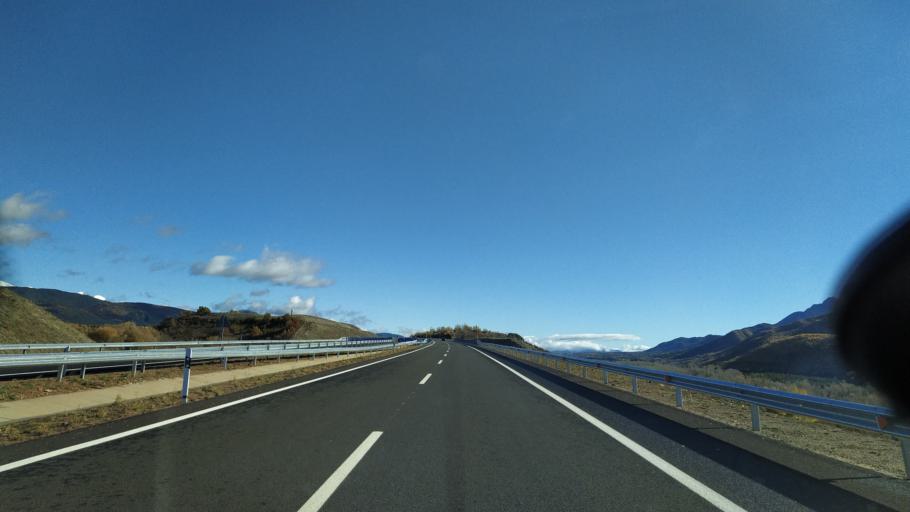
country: ES
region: Aragon
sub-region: Provincia de Huesca
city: Santa Cruz de la Seros
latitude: 42.5613
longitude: -0.6580
